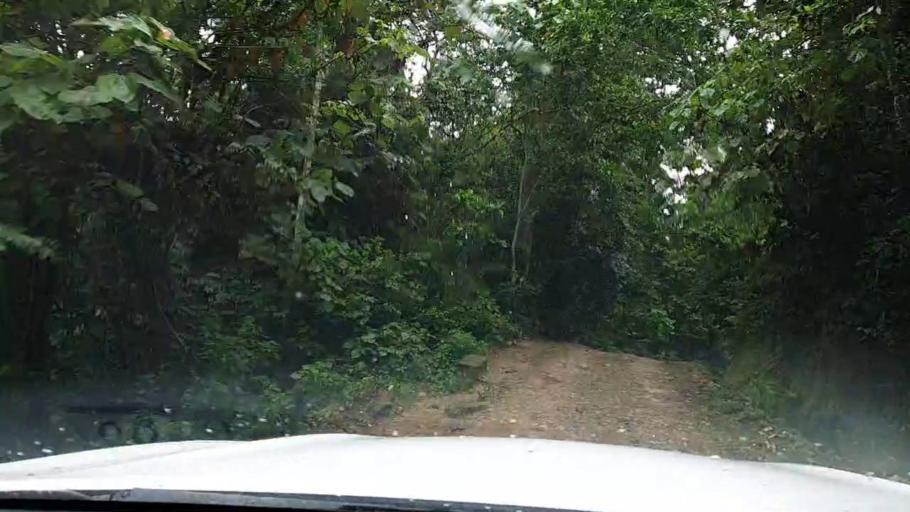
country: RW
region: Western Province
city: Cyangugu
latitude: -2.5590
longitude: 28.9857
